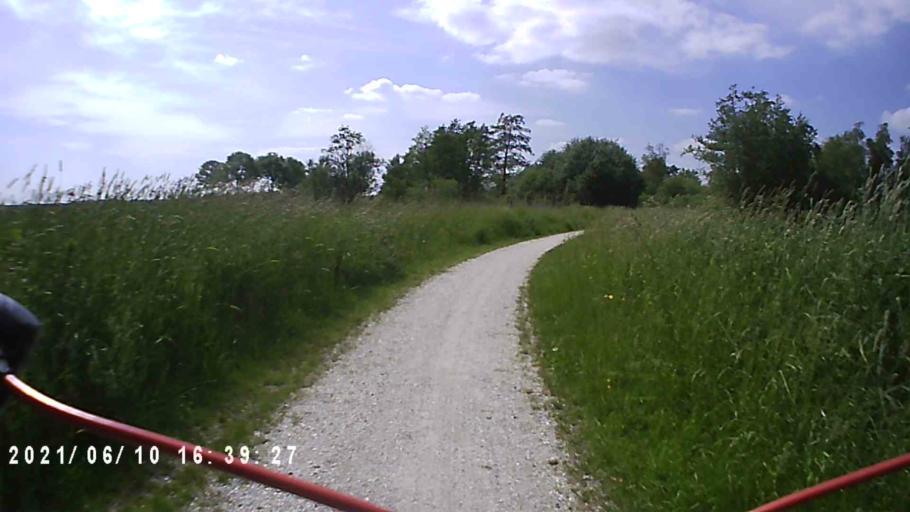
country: NL
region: Friesland
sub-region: Gemeente Achtkarspelen
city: Buitenpost
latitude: 53.2431
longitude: 6.1443
